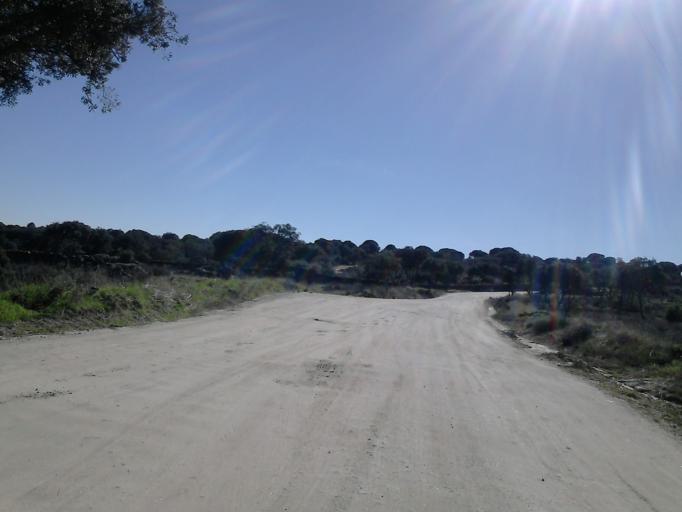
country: ES
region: Madrid
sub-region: Provincia de Madrid
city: Galapagar
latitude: 40.5596
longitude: -3.9813
